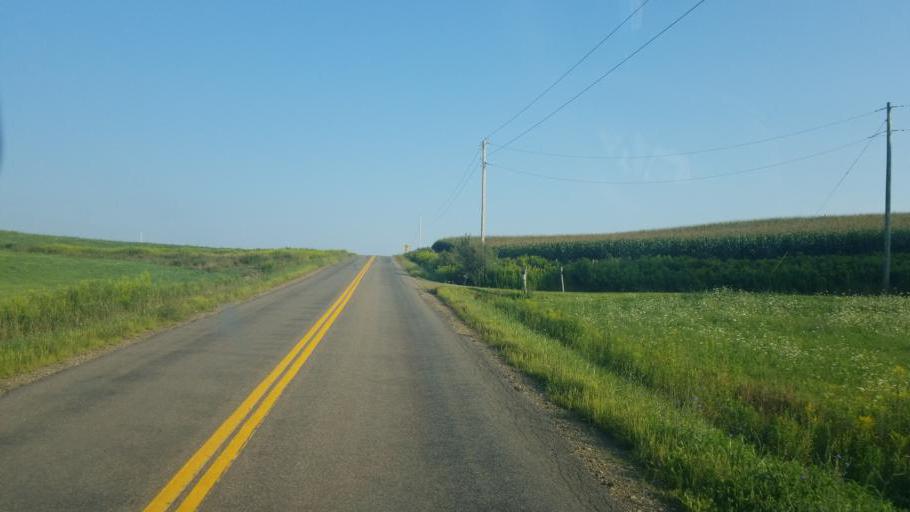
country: US
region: Pennsylvania
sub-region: Tioga County
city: Westfield
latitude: 42.0716
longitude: -77.6358
